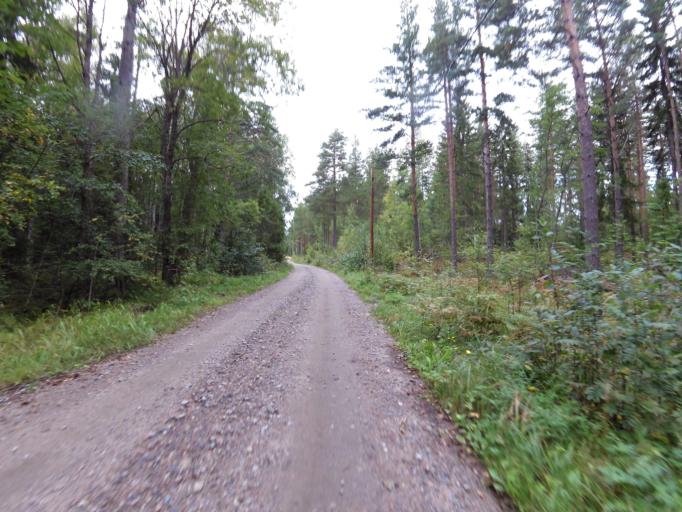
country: SE
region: Gaevleborg
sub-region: Gavle Kommun
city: Valbo
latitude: 60.7576
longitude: 16.9638
